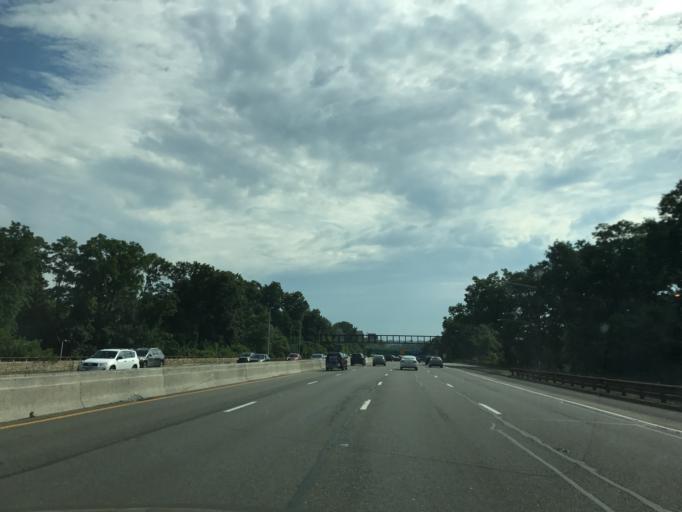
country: US
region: New Jersey
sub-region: Union County
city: Union
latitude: 40.6953
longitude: -74.2604
